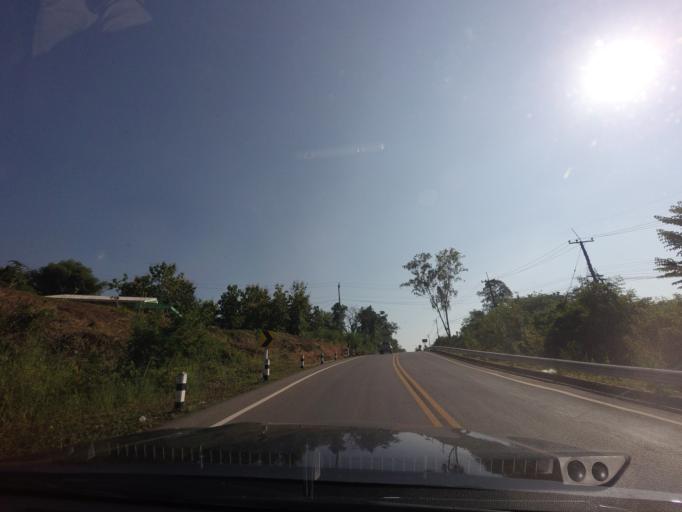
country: TH
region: Nan
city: Nan
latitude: 18.8033
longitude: 100.8002
